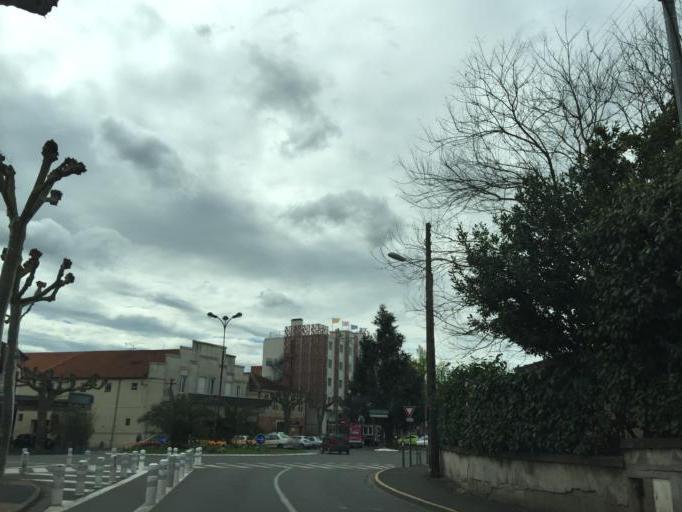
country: FR
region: Midi-Pyrenees
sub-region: Departement du Tarn
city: Albi
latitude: 43.9228
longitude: 2.1394
